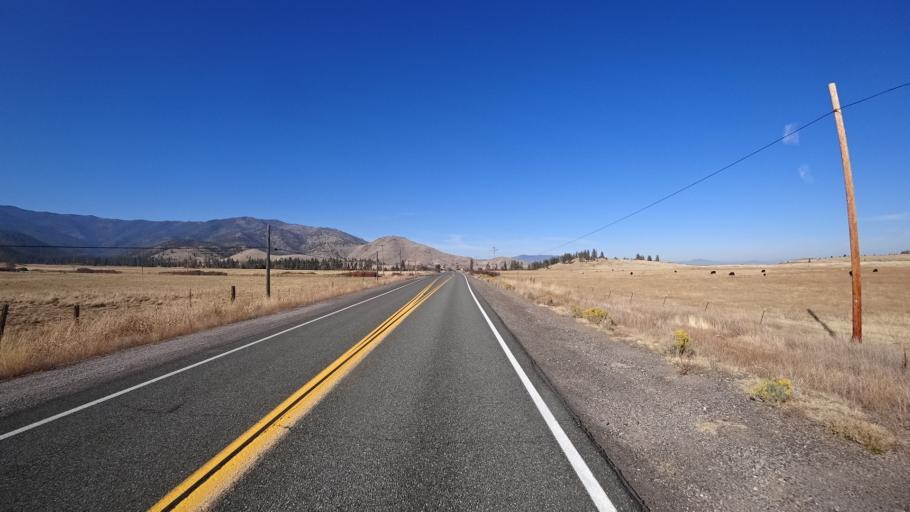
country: US
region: California
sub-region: Siskiyou County
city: Weed
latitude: 41.4435
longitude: -122.4411
